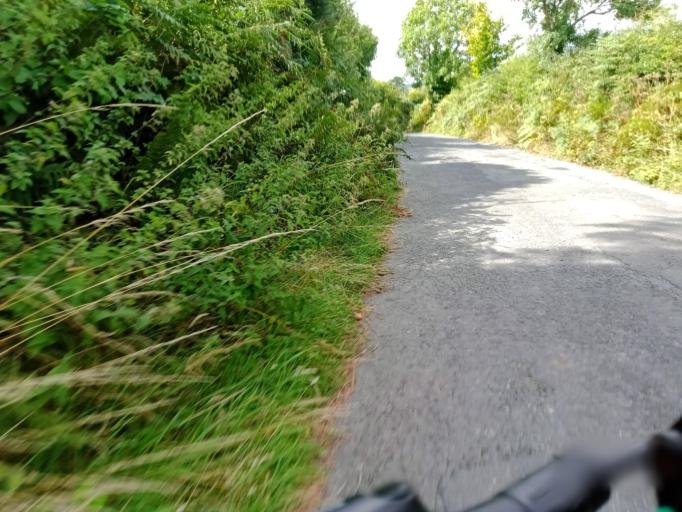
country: IE
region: Munster
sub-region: Waterford
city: Dungarvan
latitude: 52.1377
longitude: -7.4779
